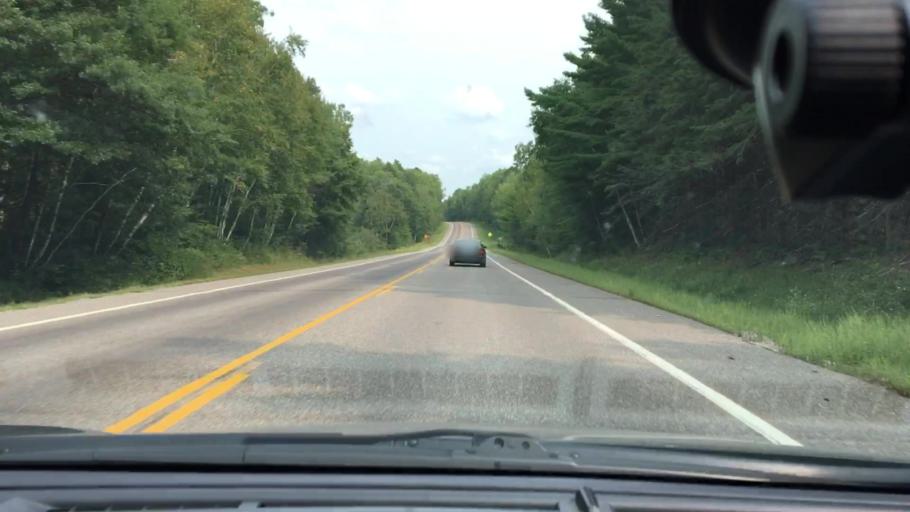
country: US
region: Minnesota
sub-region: Crow Wing County
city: Cross Lake
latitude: 46.7310
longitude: -94.0098
